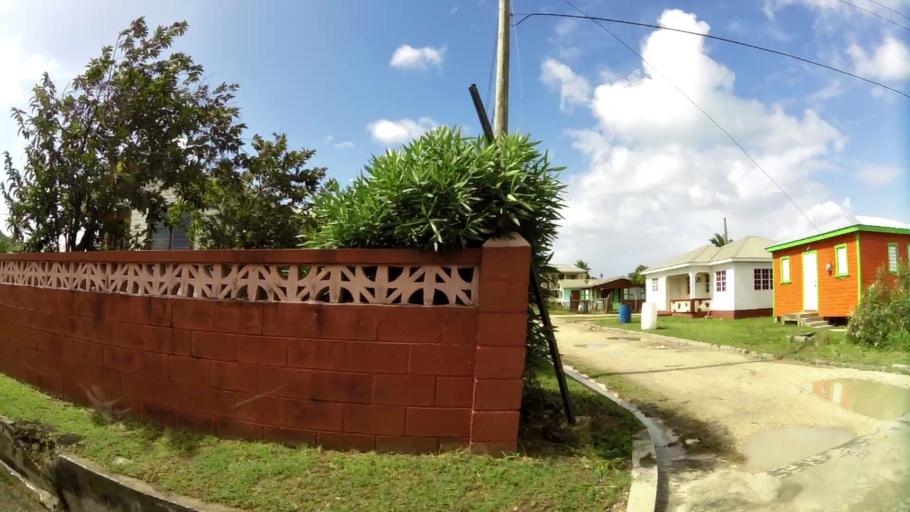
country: AG
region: Saint Mary
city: Bolands
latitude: 17.0685
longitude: -61.8761
